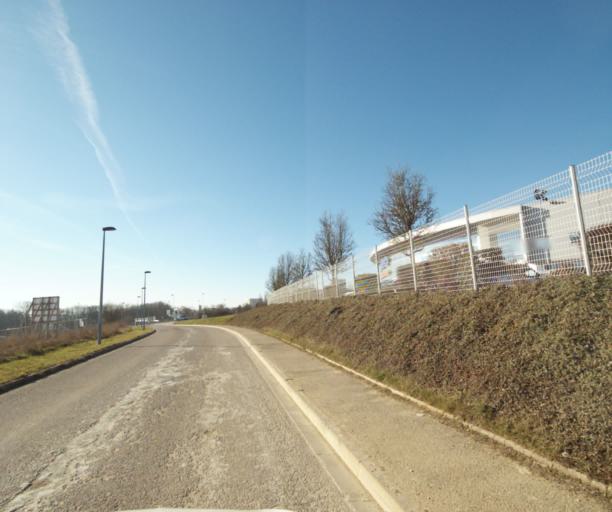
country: FR
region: Lorraine
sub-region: Departement de Meurthe-et-Moselle
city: Laxou
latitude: 48.7068
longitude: 6.1354
